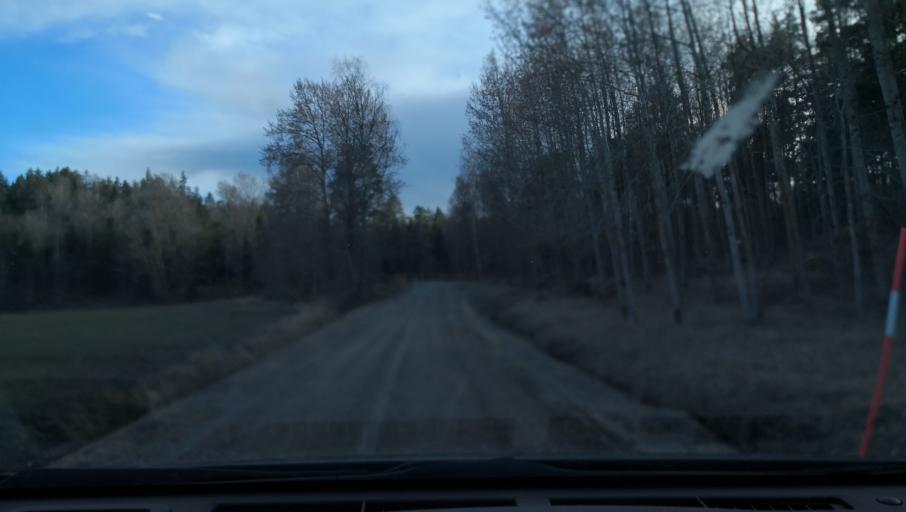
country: SE
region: Vaestmanland
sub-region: Arboga Kommun
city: Arboga
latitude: 59.4445
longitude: 15.7524
